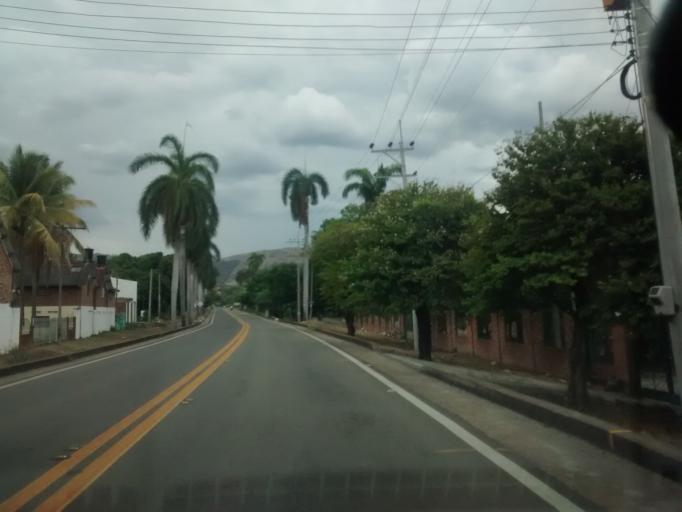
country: CO
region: Cundinamarca
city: Tocaima
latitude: 4.4518
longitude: -74.6499
